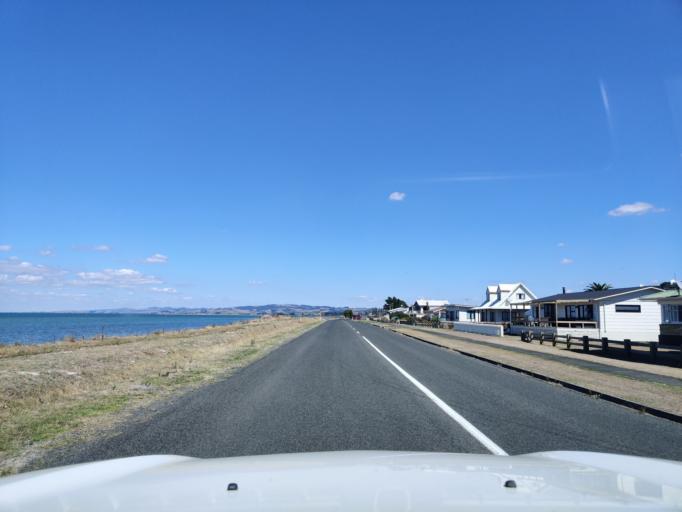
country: NZ
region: Waikato
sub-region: Thames-Coromandel District
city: Thames
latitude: -37.1068
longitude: 175.2992
